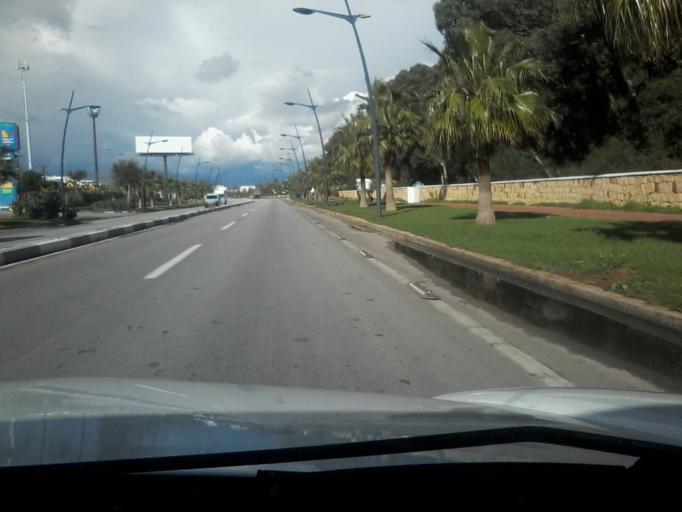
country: MA
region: Tanger-Tetouan
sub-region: Tetouan
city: Martil
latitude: 35.7359
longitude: -5.3420
